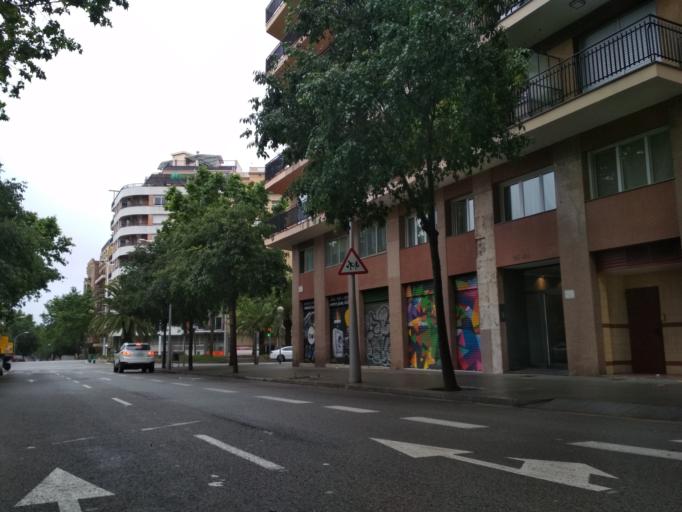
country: ES
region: Catalonia
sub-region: Provincia de Barcelona
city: Horta-Guinardo
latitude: 41.4031
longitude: 2.1827
